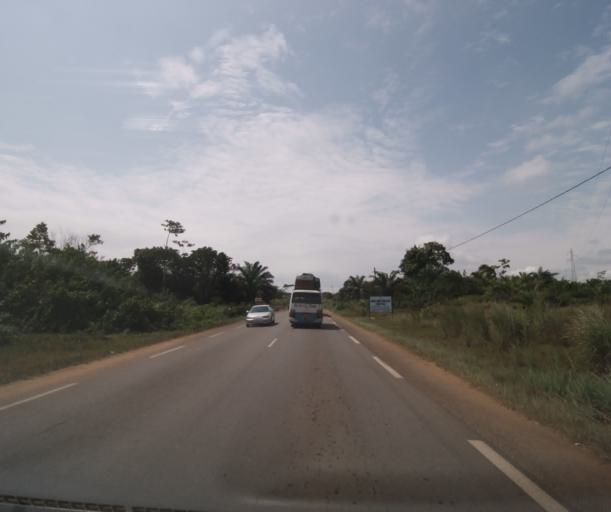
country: CM
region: South Province
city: Kribi
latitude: 2.9976
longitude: 9.9391
